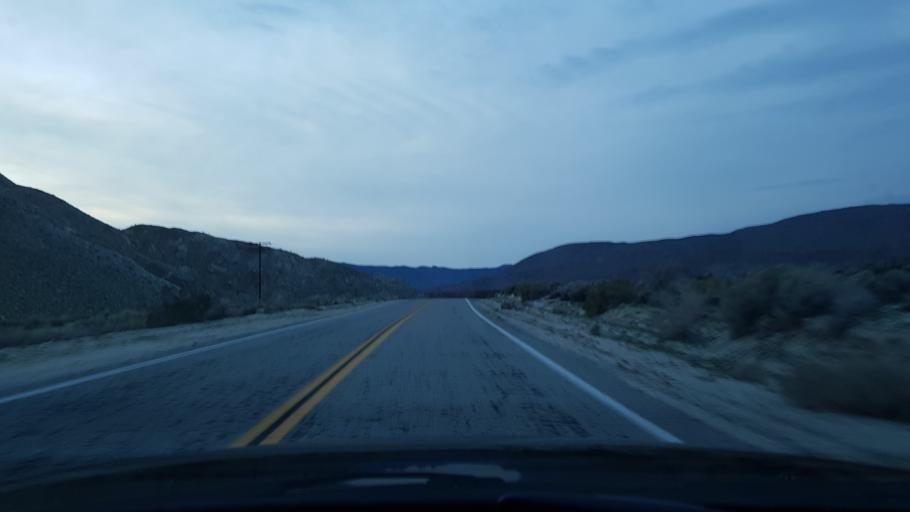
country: US
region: California
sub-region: San Diego County
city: Pine Valley
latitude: 32.9695
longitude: -116.3347
